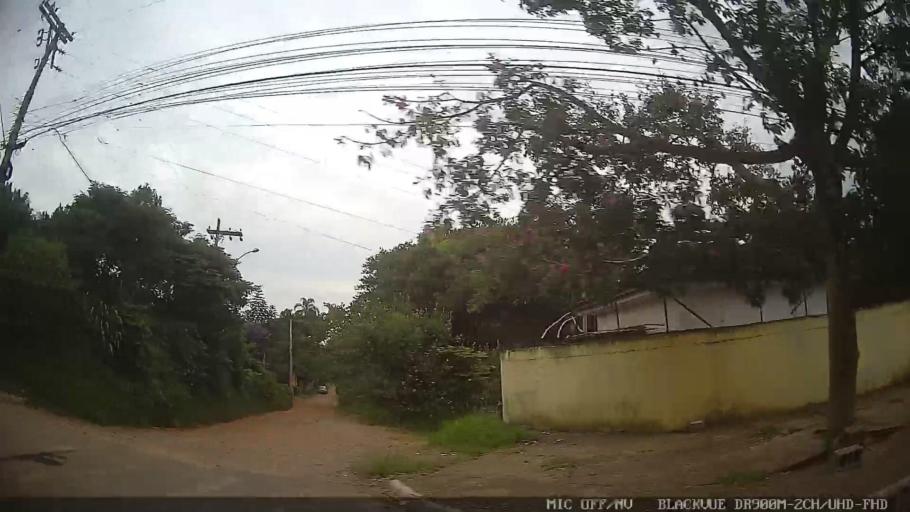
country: BR
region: Sao Paulo
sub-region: Atibaia
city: Atibaia
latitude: -23.1564
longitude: -46.5954
